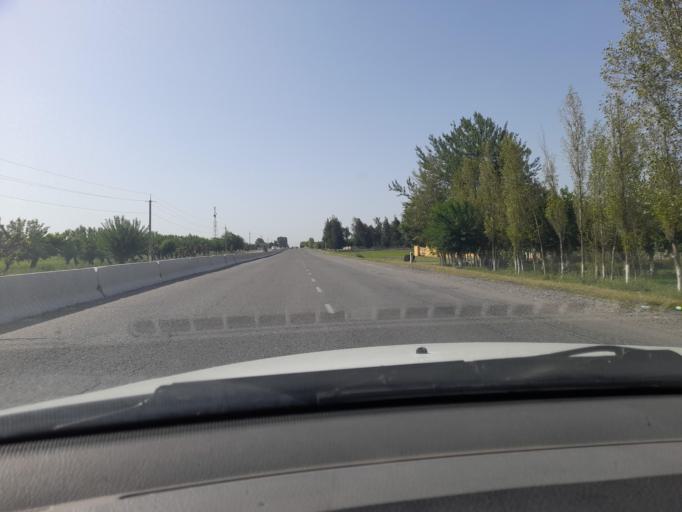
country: UZ
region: Samarqand
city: Daxbet
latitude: 39.8093
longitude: 66.8568
